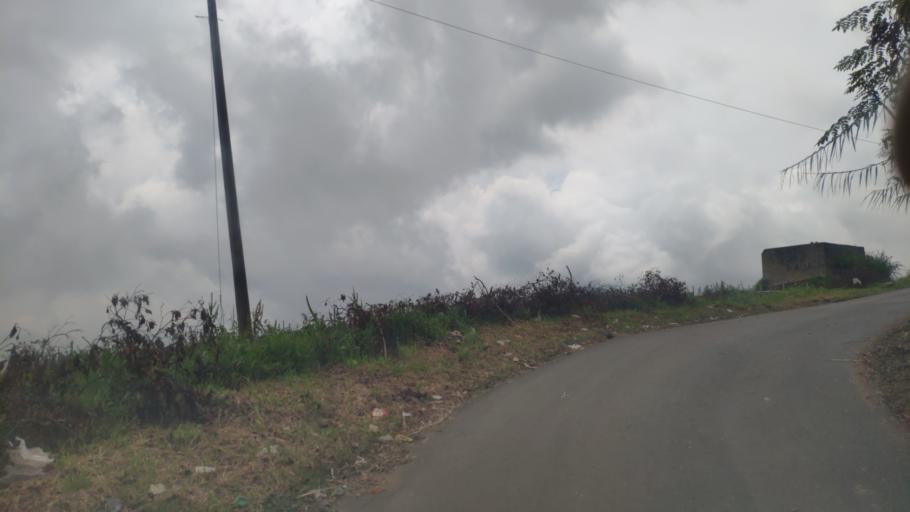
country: ID
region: Central Java
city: Wonosobo
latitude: -7.1917
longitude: 109.8154
